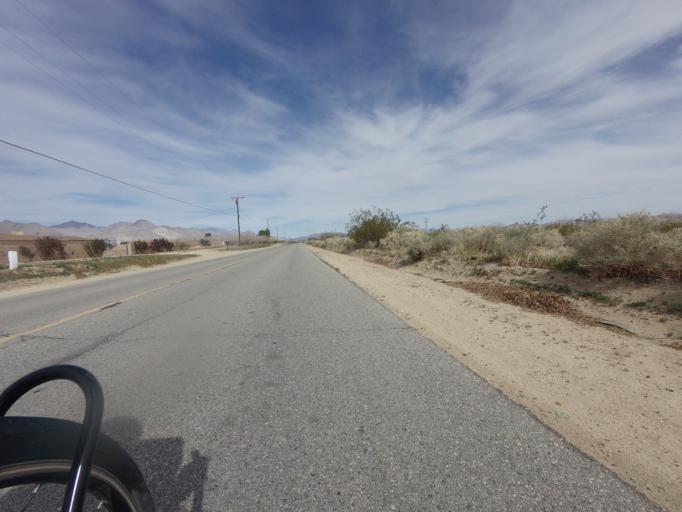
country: US
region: California
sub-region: Kern County
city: Inyokern
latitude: 35.7037
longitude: -117.8291
